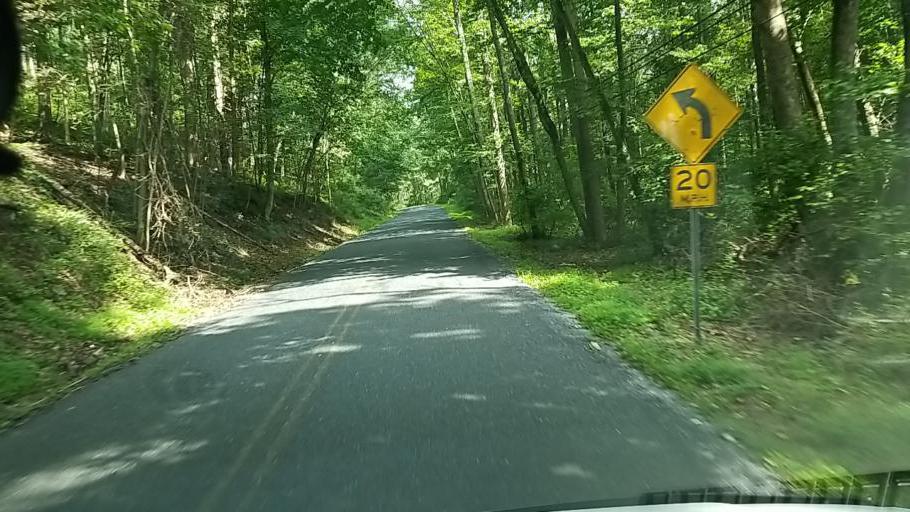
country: US
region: Pennsylvania
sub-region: Dauphin County
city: Millersburg
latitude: 40.5126
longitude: -76.9245
